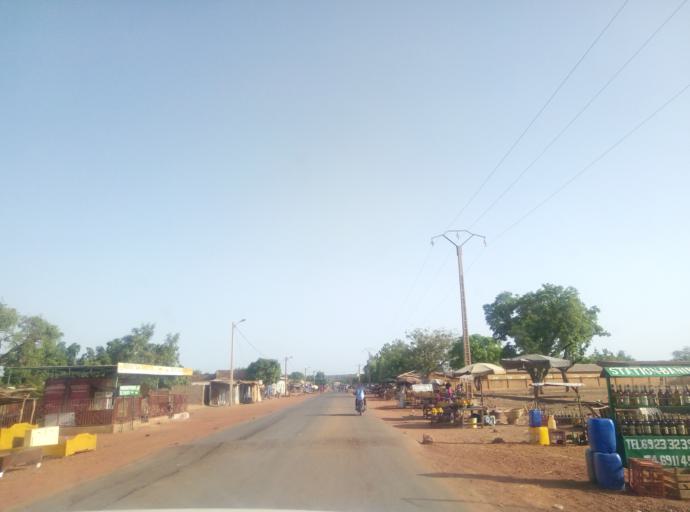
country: ML
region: Bamako
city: Bamako
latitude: 12.5917
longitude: -7.7666
